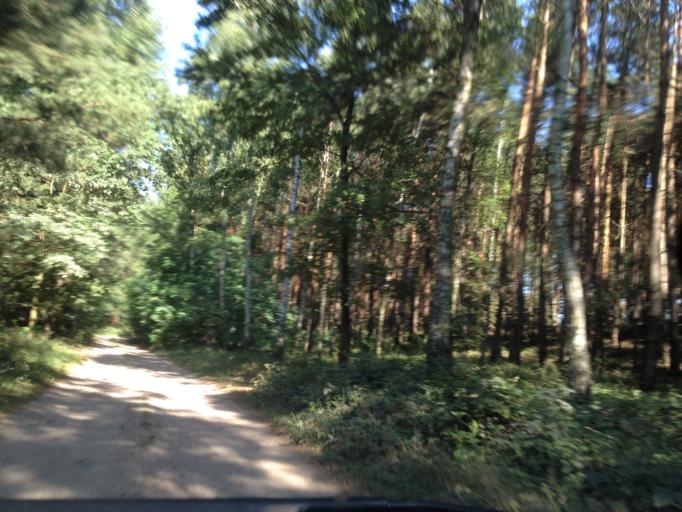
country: PL
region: Greater Poland Voivodeship
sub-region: Powiat sredzki
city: Zaniemysl
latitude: 52.1052
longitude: 17.1301
